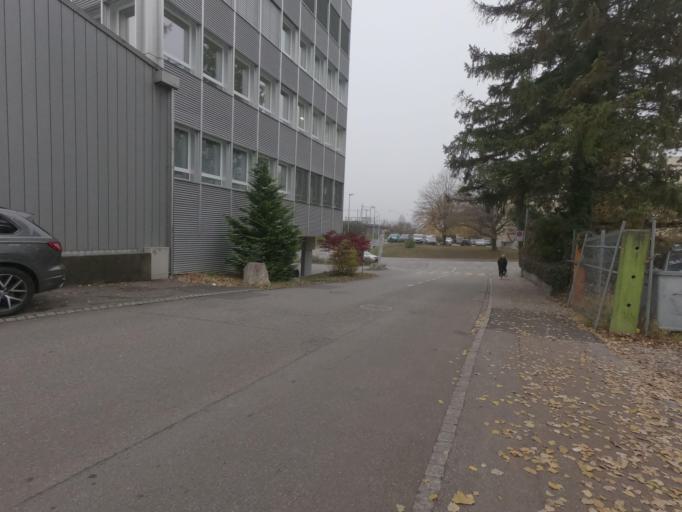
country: CH
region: Solothurn
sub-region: Bezirk Lebern
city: Grenchen
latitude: 47.1906
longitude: 7.4047
